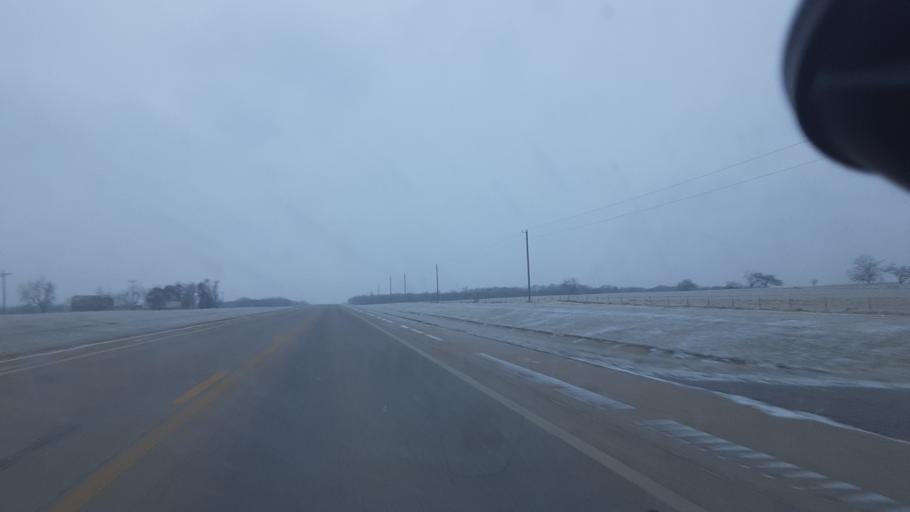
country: US
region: Oklahoma
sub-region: Payne County
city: Perkins
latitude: 35.9859
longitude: -97.1319
